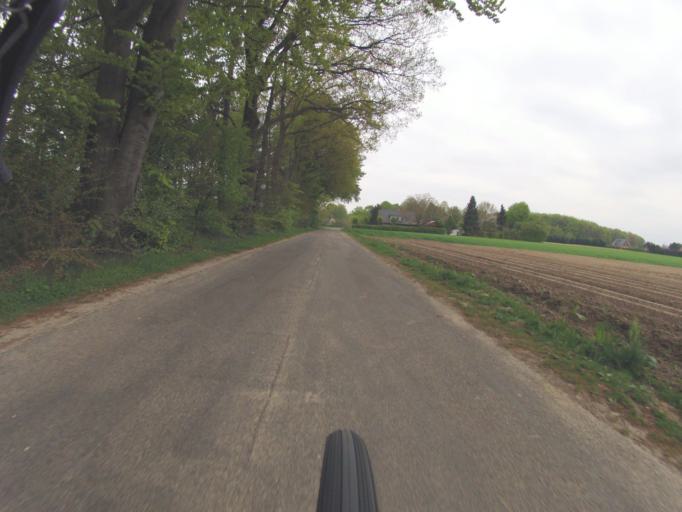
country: DE
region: North Rhine-Westphalia
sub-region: Regierungsbezirk Munster
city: Mettingen
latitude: 52.2965
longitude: 7.7890
